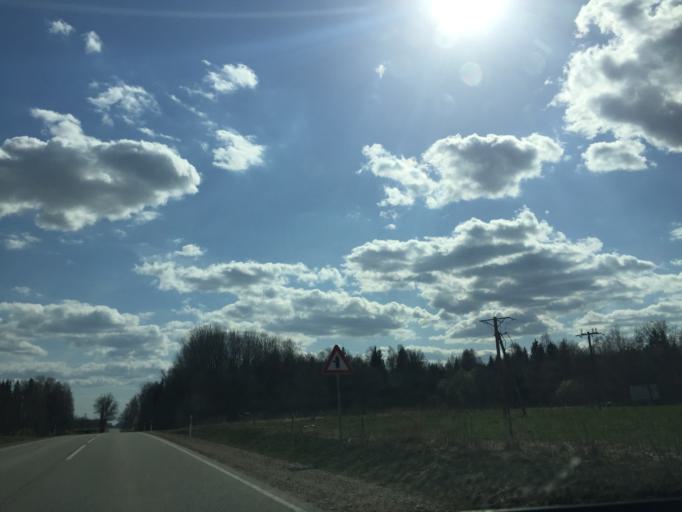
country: LV
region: Skriveri
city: Skriveri
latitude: 56.7451
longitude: 25.1667
